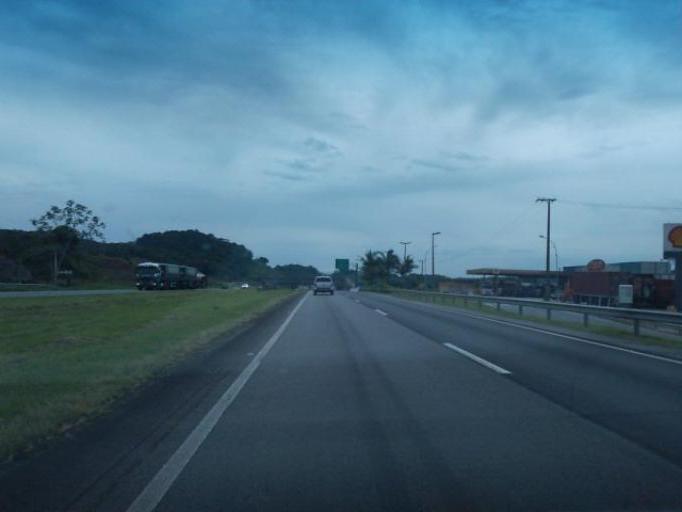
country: BR
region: Sao Paulo
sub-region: Juquia
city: Juquia
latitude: -24.3308
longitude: -47.6289
